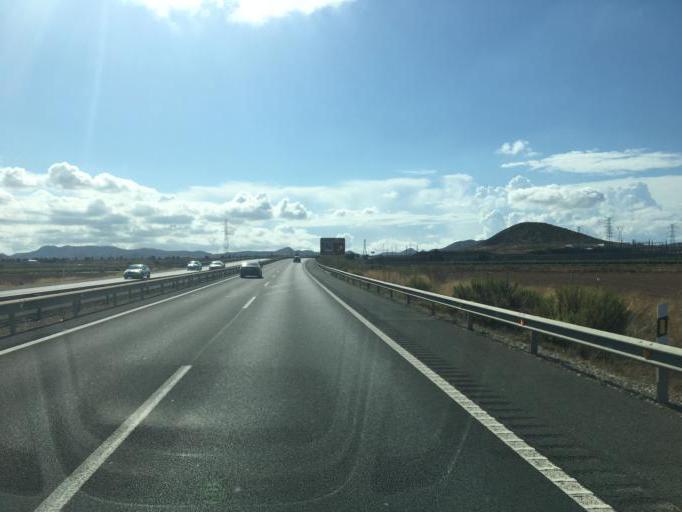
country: ES
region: Murcia
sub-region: Murcia
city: Cartagena
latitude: 37.6417
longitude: -0.9640
